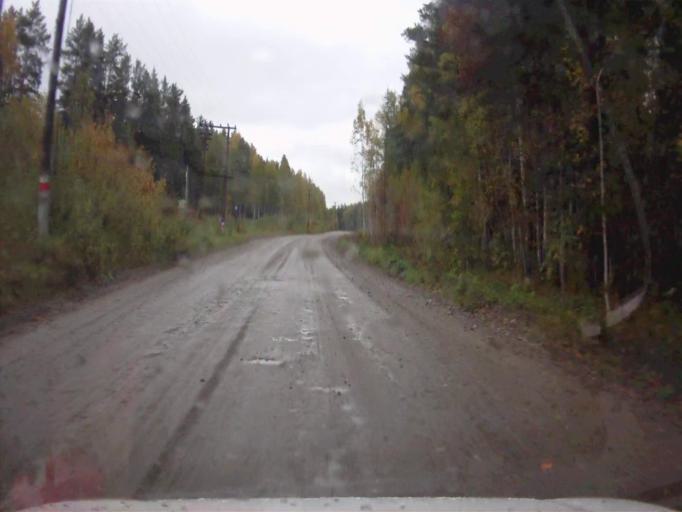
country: RU
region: Chelyabinsk
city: Kyshtym
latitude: 55.8014
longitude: 60.4798
